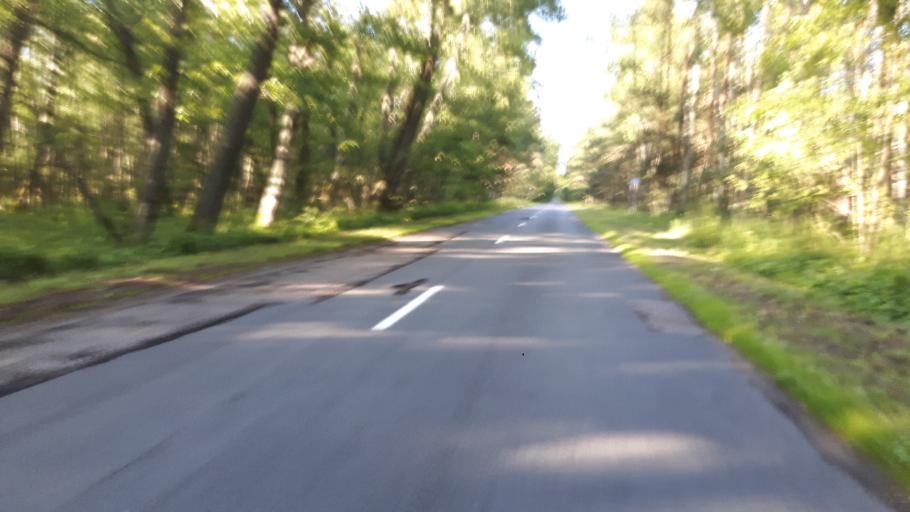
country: LT
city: Nida
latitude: 55.2276
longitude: 20.8982
